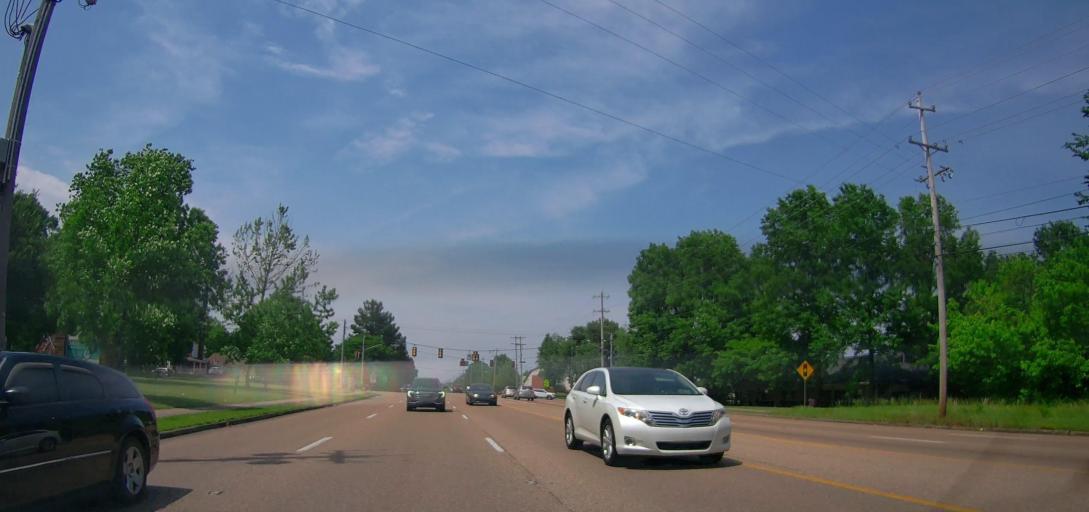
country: US
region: Tennessee
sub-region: Shelby County
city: Germantown
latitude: 35.0271
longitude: -89.7958
